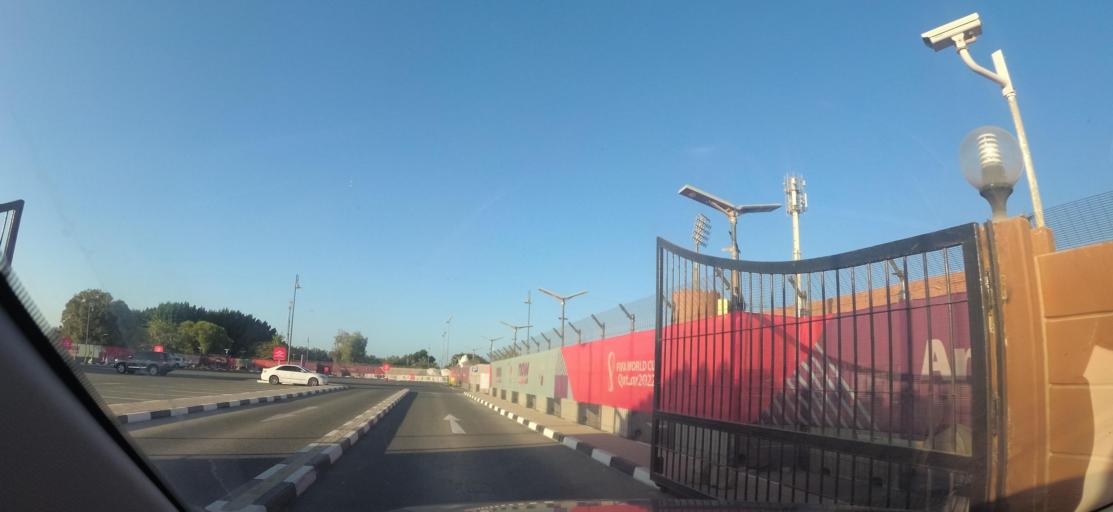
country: QA
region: Madinat ash Shamal
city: Ar Ru'ays
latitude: 26.1176
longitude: 51.2198
